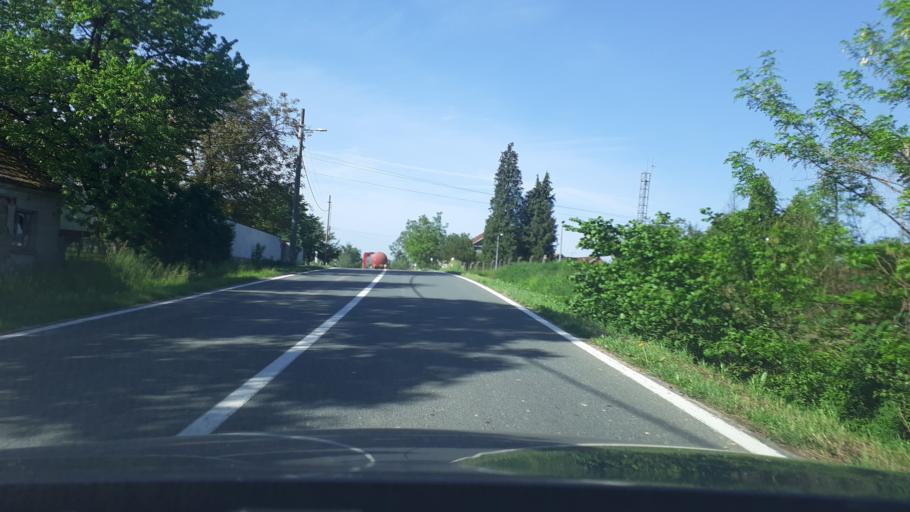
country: HR
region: Brodsko-Posavska
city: Batrina
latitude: 45.1971
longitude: 17.6644
